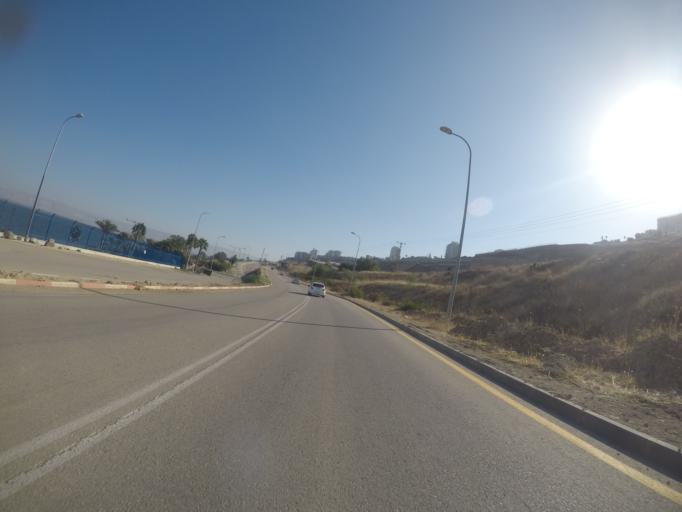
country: IL
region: Northern District
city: Tiberias
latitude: 32.8054
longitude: 35.5275
